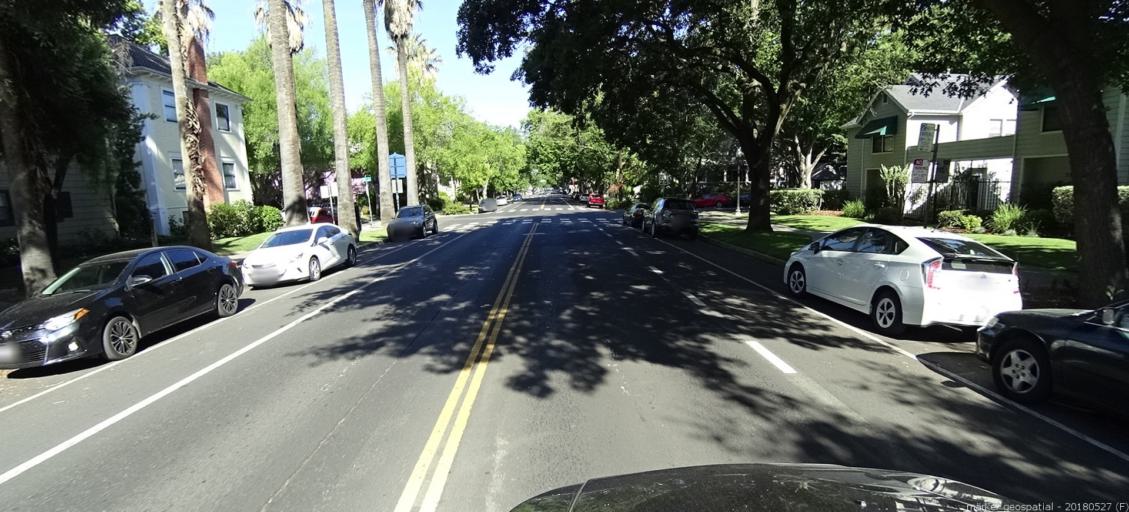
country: US
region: California
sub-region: Sacramento County
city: Sacramento
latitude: 38.5713
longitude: -121.4786
